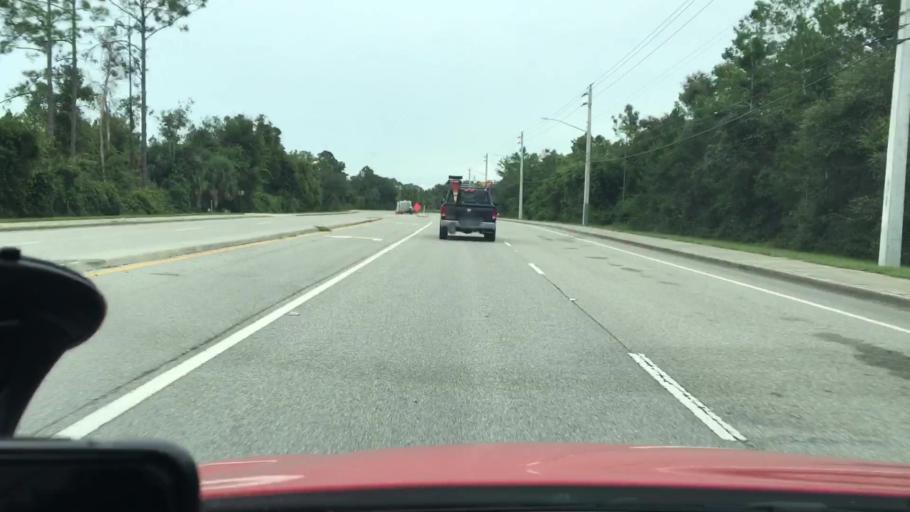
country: US
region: Florida
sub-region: Flagler County
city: Flagler Beach
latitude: 29.4898
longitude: -81.1872
